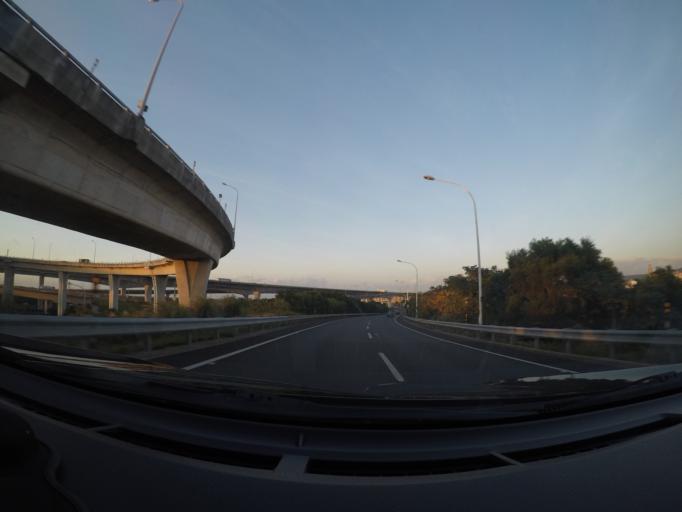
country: TW
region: Taiwan
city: Taoyuan City
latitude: 25.0183
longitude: 121.2765
